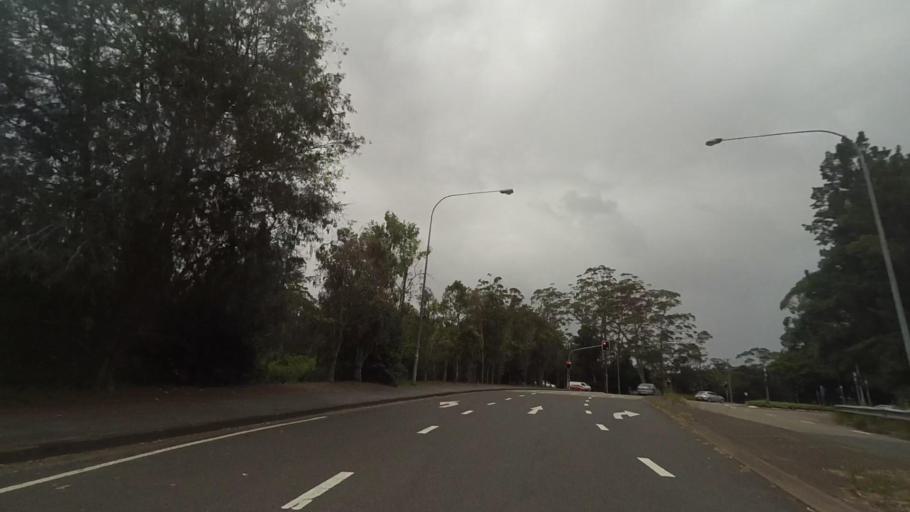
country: AU
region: New South Wales
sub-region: Wyong Shire
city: Berkeley Vale
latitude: -33.3419
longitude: 151.4278
